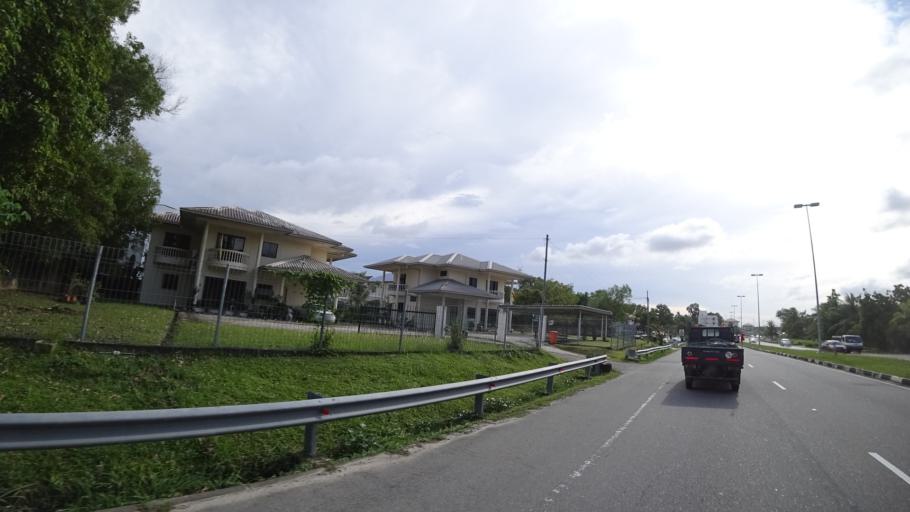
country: BN
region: Brunei and Muara
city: Bandar Seri Begawan
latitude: 4.8790
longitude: 114.8656
